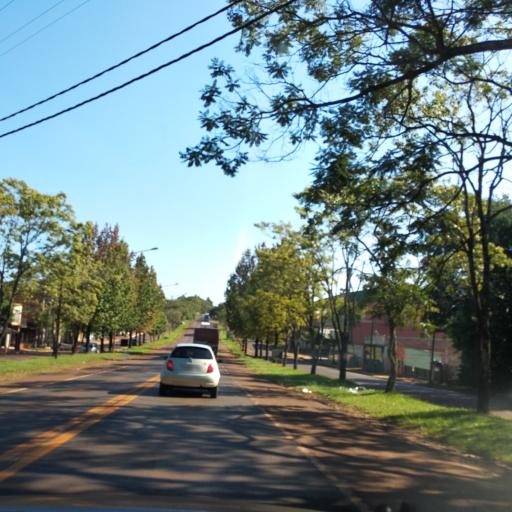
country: AR
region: Misiones
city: Jardin America
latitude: -27.0406
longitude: -55.2316
